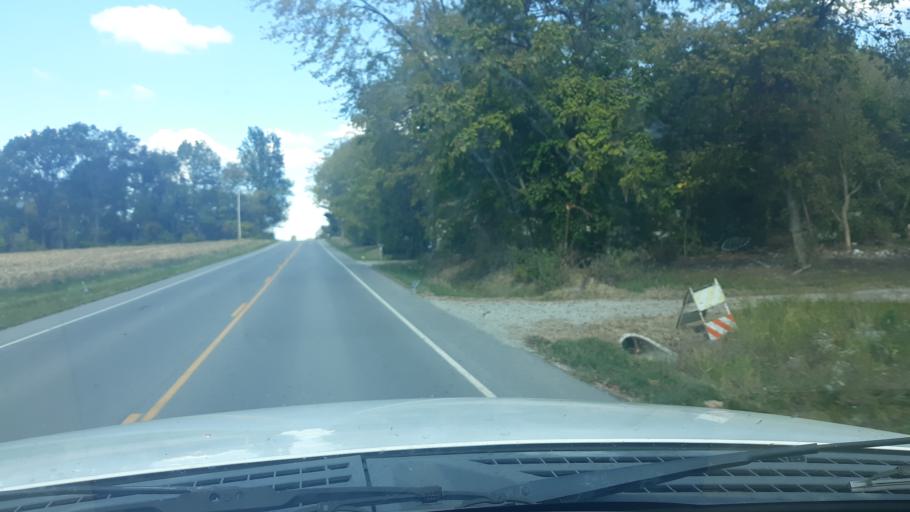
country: US
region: Illinois
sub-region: Saline County
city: Eldorado
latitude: 37.8141
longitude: -88.4848
